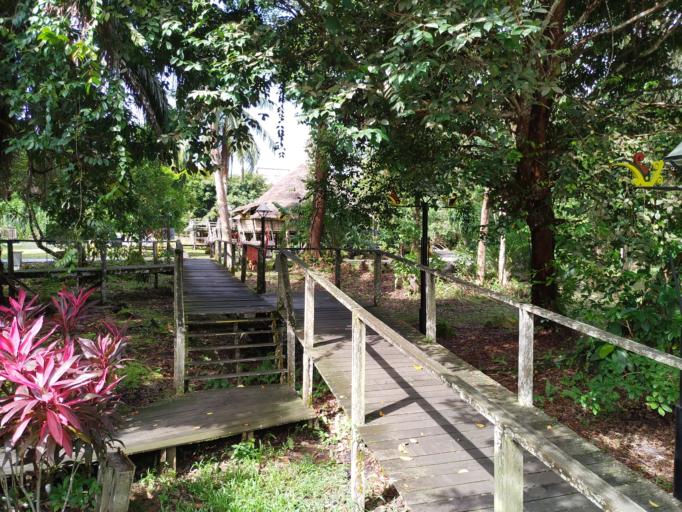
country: MY
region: Sarawak
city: Kuching
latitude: 1.7496
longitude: 110.3177
